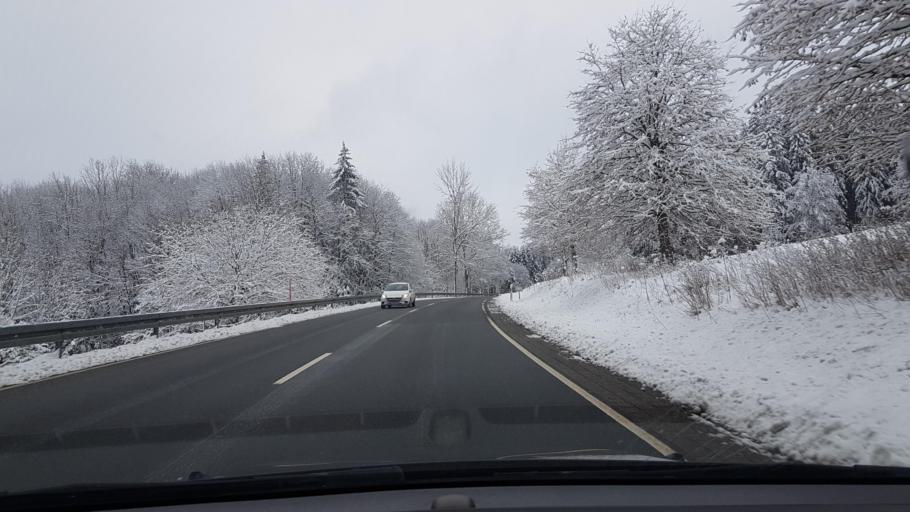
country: DE
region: Lower Saxony
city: Clausthal-Zellerfeld
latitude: 51.8056
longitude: 10.3156
